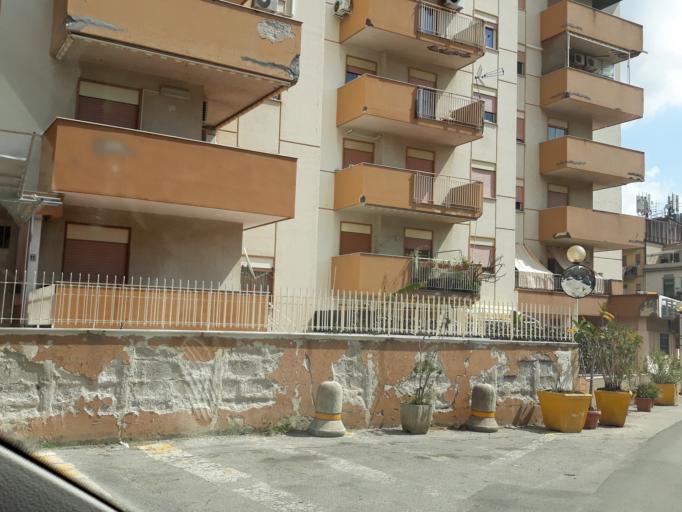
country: IT
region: Sicily
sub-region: Palermo
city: Monreale
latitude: 38.0968
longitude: 13.3135
